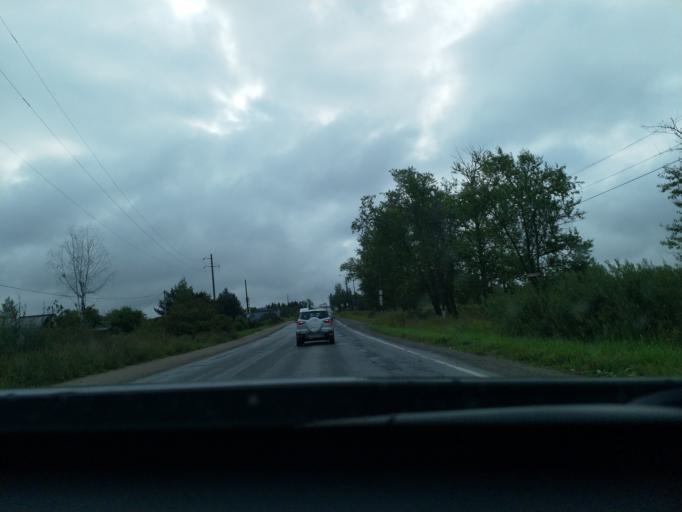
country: RU
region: Leningrad
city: Nikol'skoye
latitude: 59.6918
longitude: 30.8032
